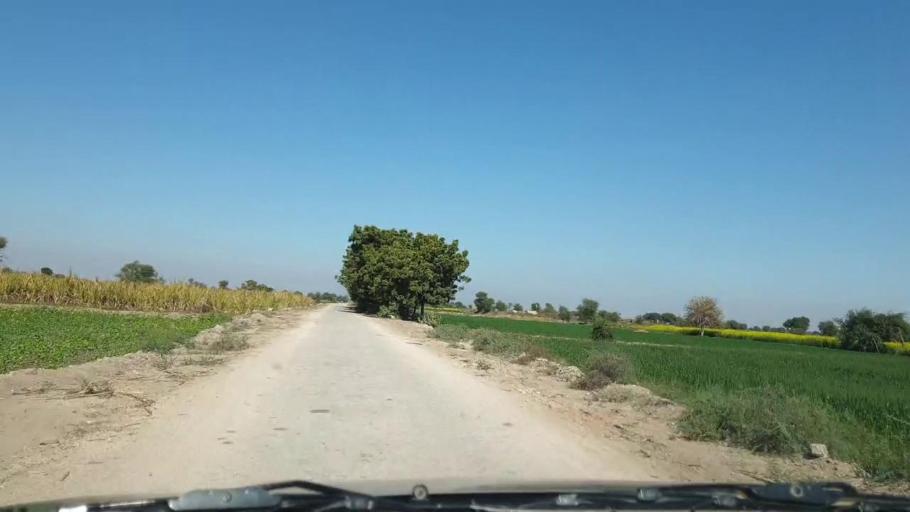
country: PK
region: Sindh
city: Khadro
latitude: 26.1424
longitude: 68.8157
